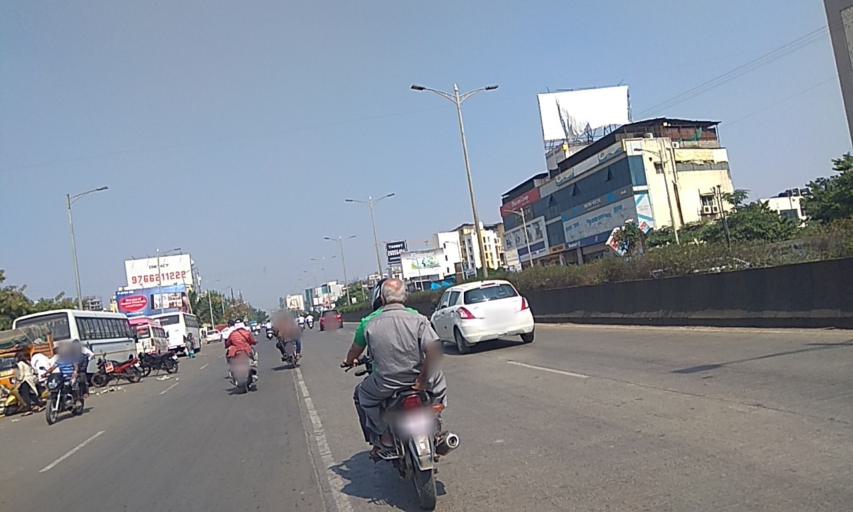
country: IN
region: Maharashtra
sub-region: Pune Division
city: Lohogaon
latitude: 18.5456
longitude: 73.9359
